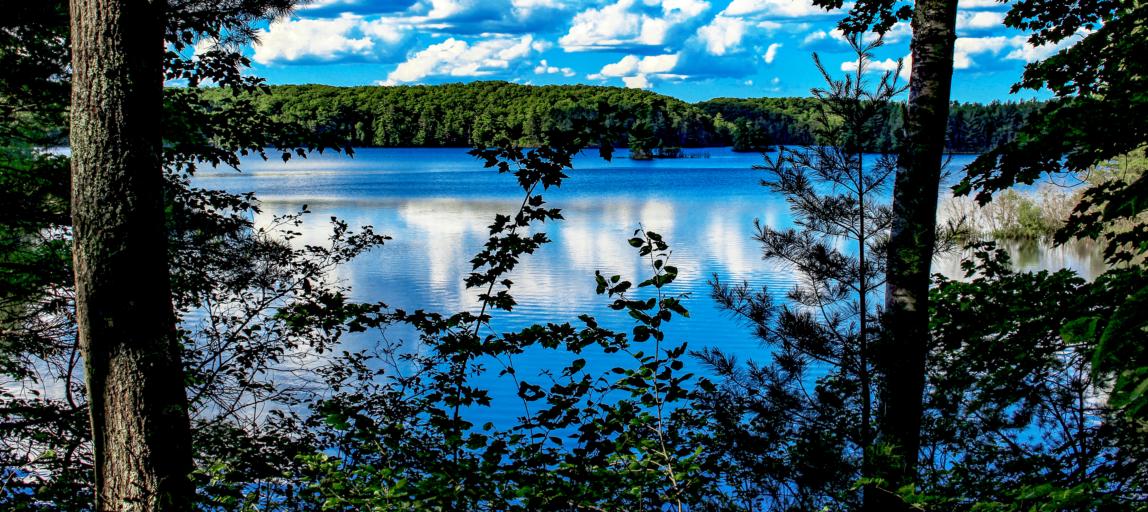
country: US
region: Wisconsin
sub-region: Vilas County
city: Eagle River
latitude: 46.0274
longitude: -89.5551
